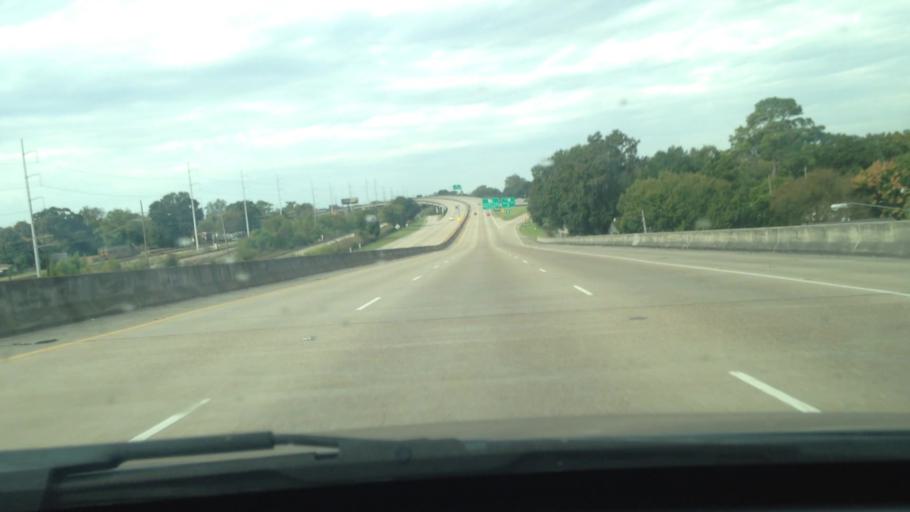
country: US
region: Louisiana
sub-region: Jefferson Parish
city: Metairie Terrace
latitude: 29.9711
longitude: -90.1637
